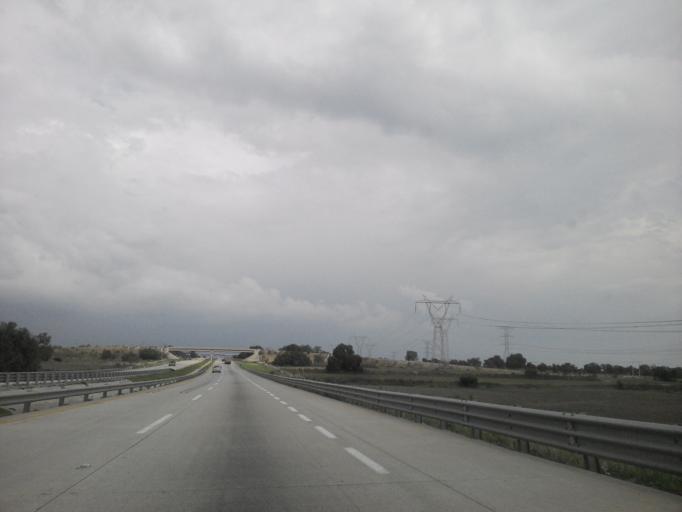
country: MX
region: Mexico
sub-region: Apaxco
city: Colonia Juarez
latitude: 19.9924
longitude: -99.1322
